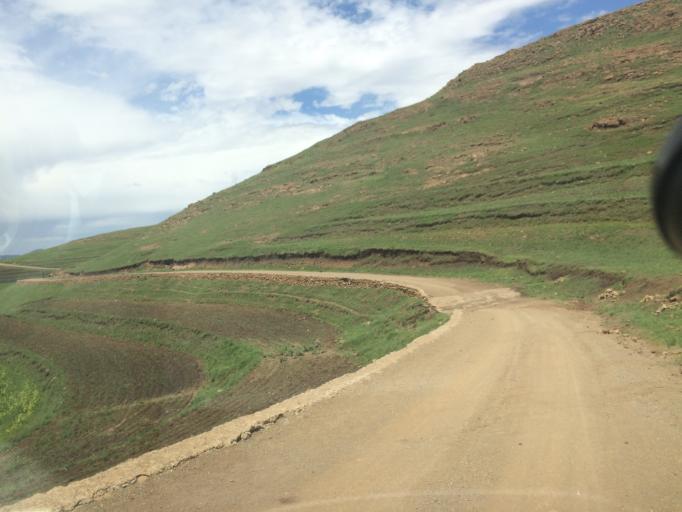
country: LS
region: Maseru
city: Nako
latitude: -29.8696
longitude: 28.0399
